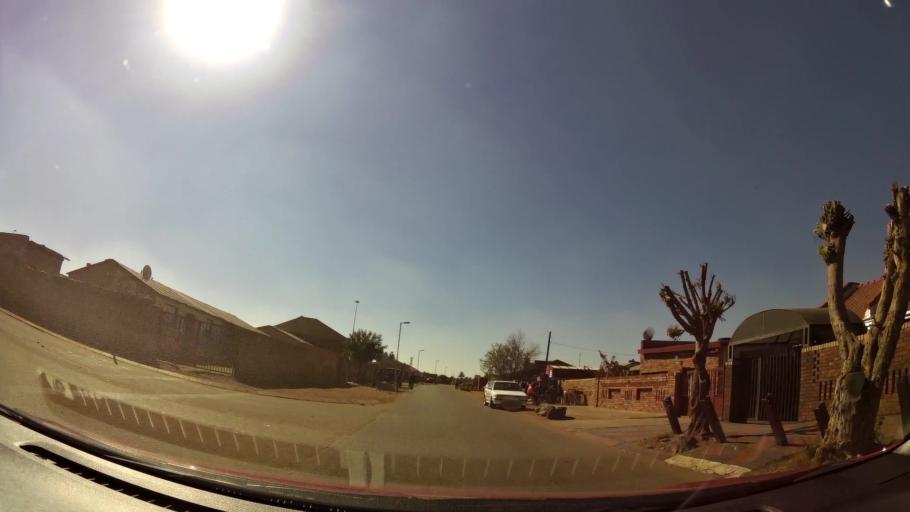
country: ZA
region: Gauteng
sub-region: City of Johannesburg Metropolitan Municipality
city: Soweto
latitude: -26.2377
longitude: 27.8409
